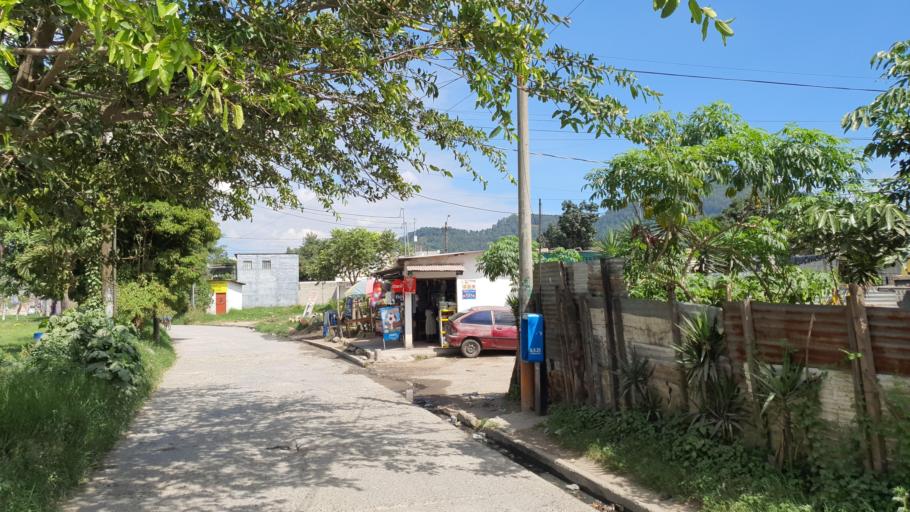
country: GT
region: Guatemala
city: Villa Canales
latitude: 14.4608
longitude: -90.5590
